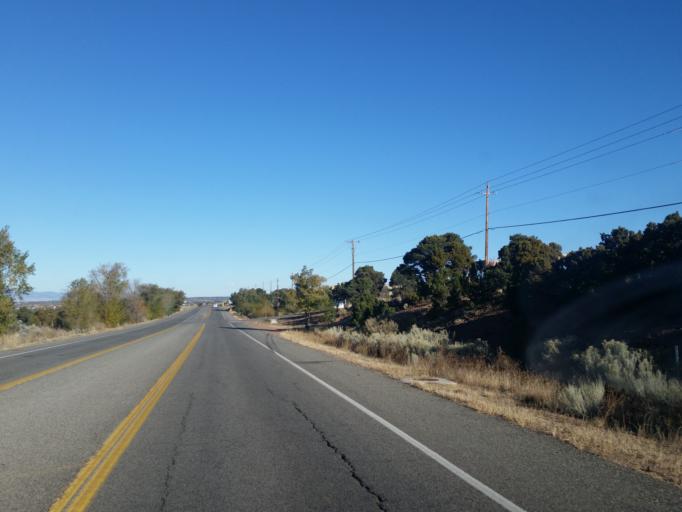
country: US
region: New Mexico
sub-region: Santa Fe County
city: Santa Fe
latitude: 35.6313
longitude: -105.9239
